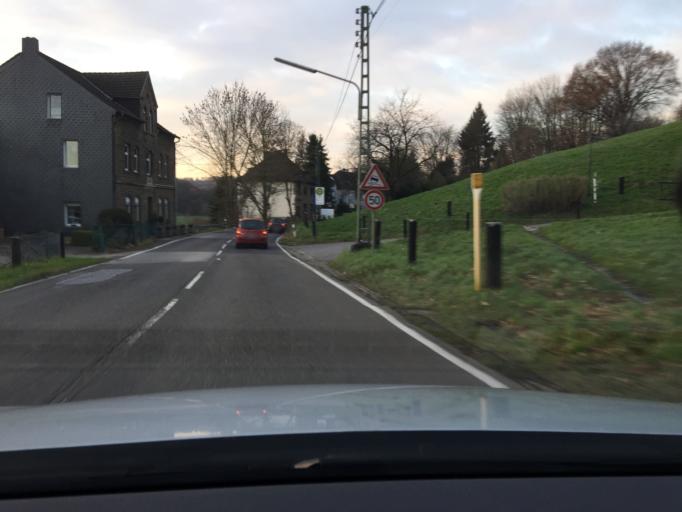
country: DE
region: North Rhine-Westphalia
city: Hattingen
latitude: 51.3785
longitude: 7.1262
